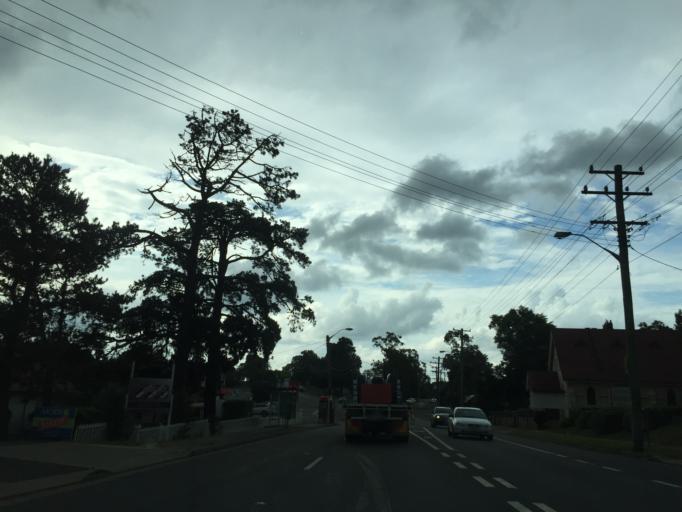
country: AU
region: New South Wales
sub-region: The Hills Shire
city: Glenhaven
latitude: -33.6828
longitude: 151.0282
